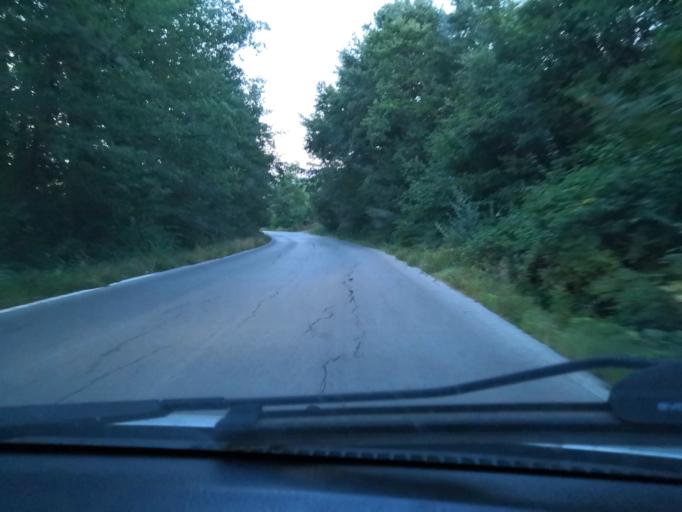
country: IT
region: Molise
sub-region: Provincia di Campobasso
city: Jelsi
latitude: 41.5109
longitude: 14.7801
